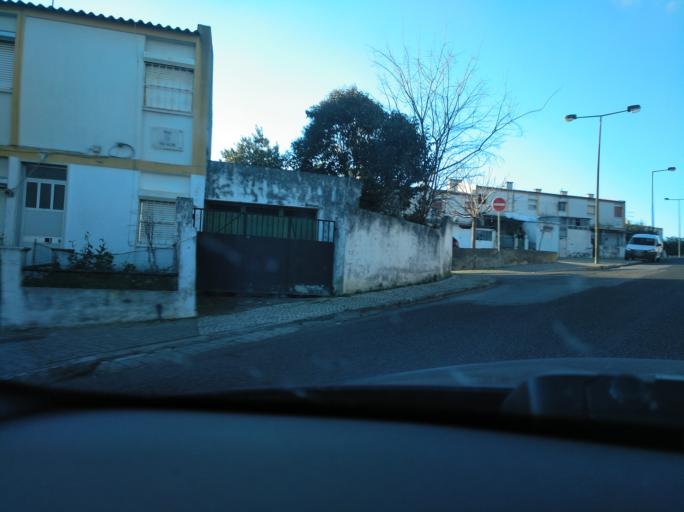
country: PT
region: Lisbon
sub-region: Odivelas
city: Pontinha
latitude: 38.7725
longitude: -9.1875
